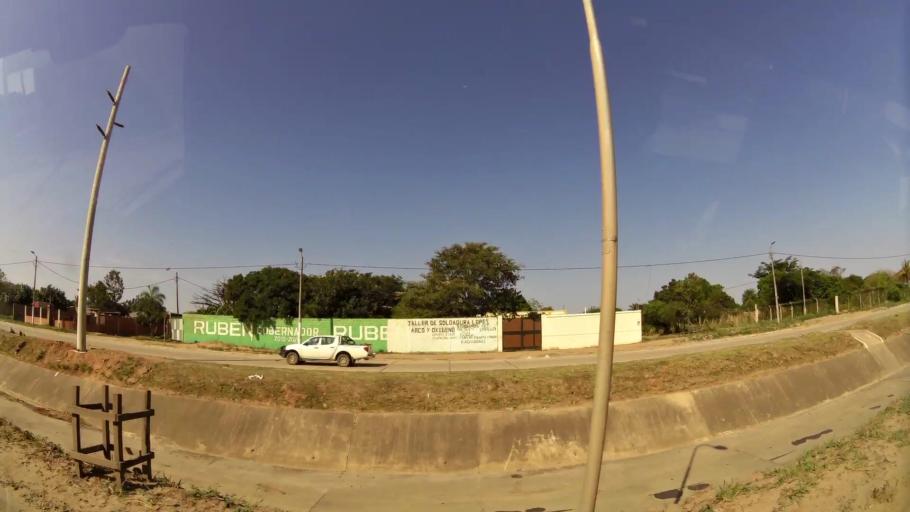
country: BO
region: Santa Cruz
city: Cotoca
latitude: -17.8063
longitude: -63.1094
